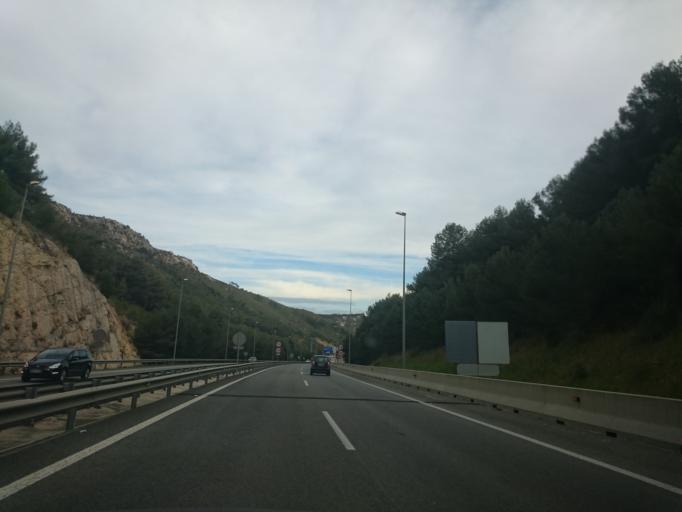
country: ES
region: Catalonia
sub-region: Provincia de Barcelona
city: Sitges
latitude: 41.2460
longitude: 1.8453
